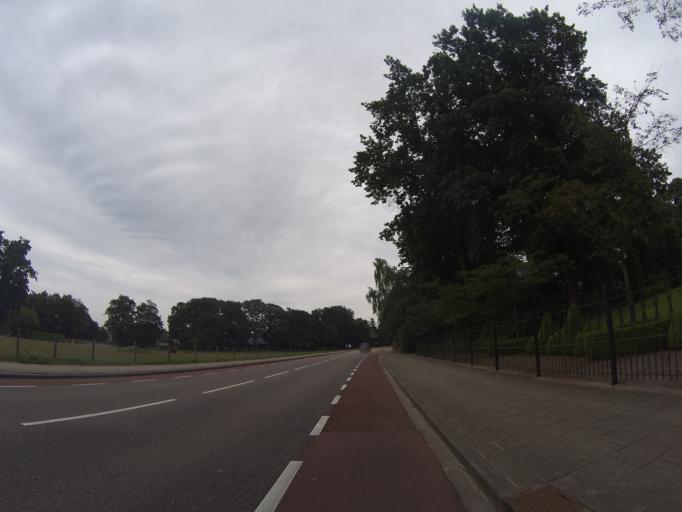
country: NL
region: Utrecht
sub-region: Gemeente Baarn
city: Baarn
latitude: 52.2184
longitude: 5.2727
